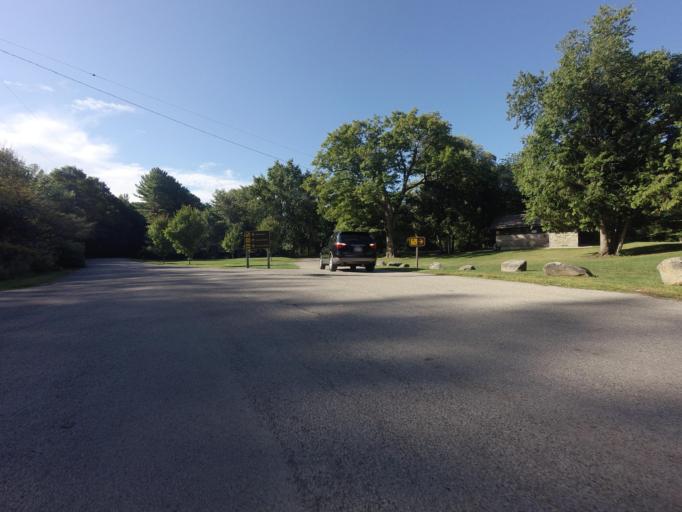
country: CA
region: Ontario
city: Waterloo
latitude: 43.6689
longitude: -80.4501
